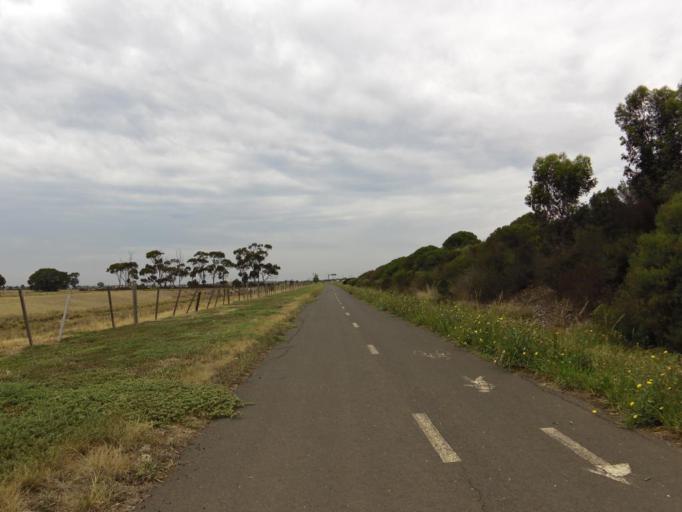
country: AU
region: Victoria
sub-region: Brimbank
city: Derrimut
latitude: -37.7826
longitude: 144.7482
